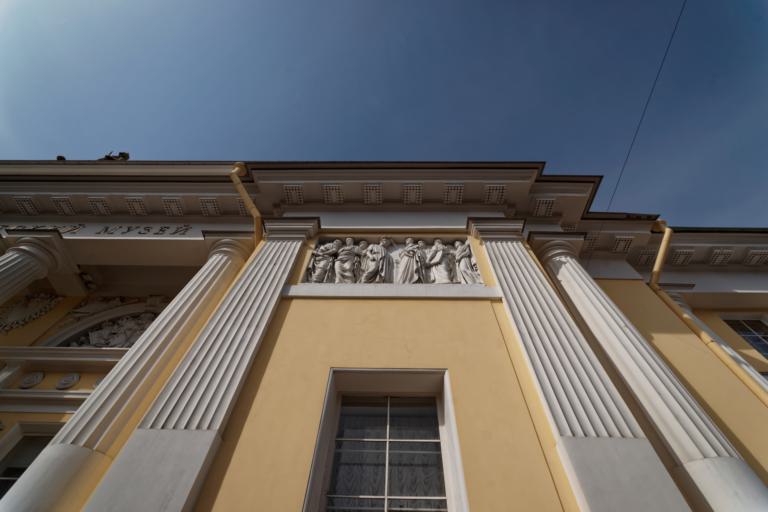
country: RU
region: St.-Petersburg
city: Saint Petersburg
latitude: 59.9377
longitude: 30.3345
